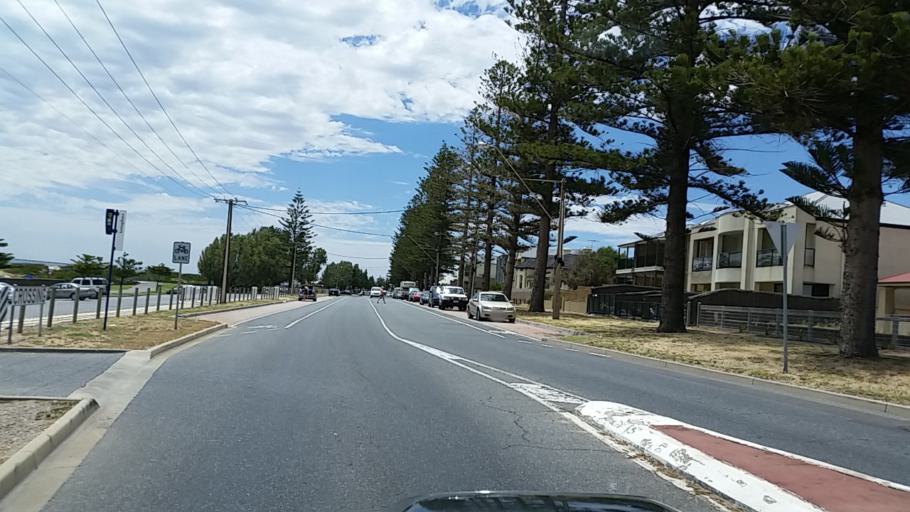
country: AU
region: South Australia
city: Port Adelaide
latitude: -34.8434
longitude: 138.4785
